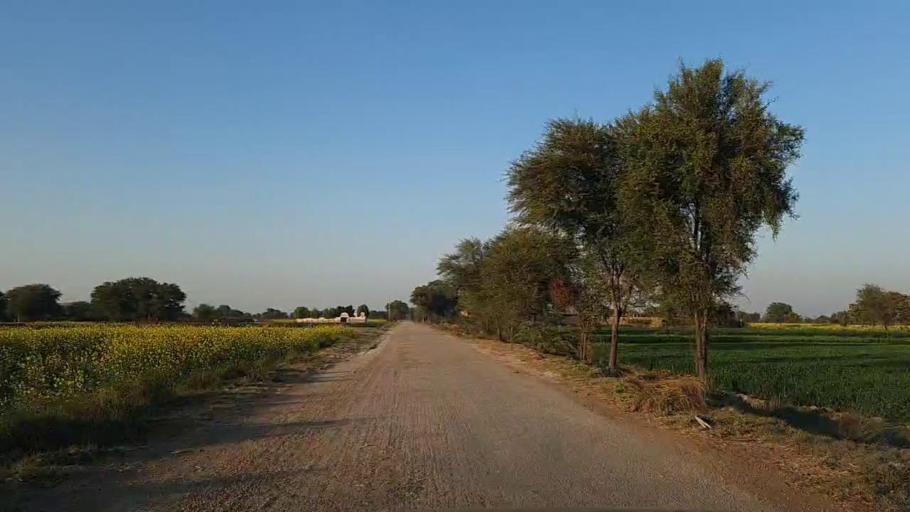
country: PK
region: Sindh
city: Nawabshah
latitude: 26.2266
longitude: 68.3380
